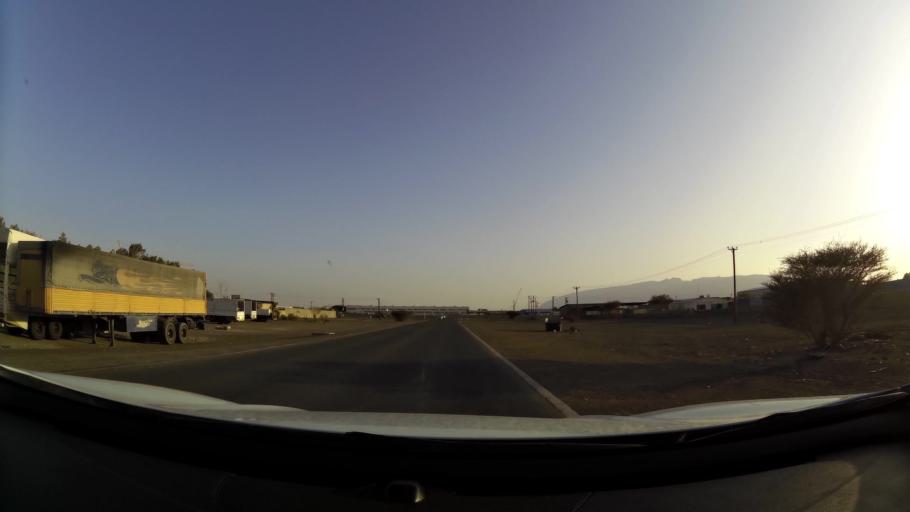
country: AE
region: Abu Dhabi
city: Al Ain
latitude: 24.1522
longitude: 55.8244
